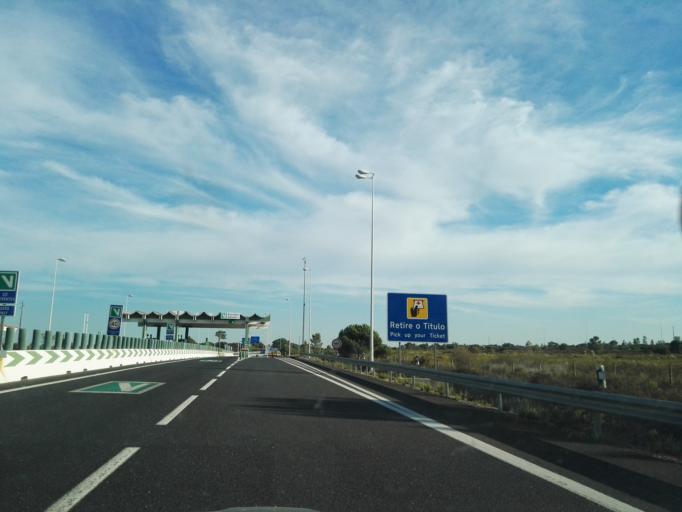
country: PT
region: Santarem
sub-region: Benavente
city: Poceirao
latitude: 38.8415
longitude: -8.7286
